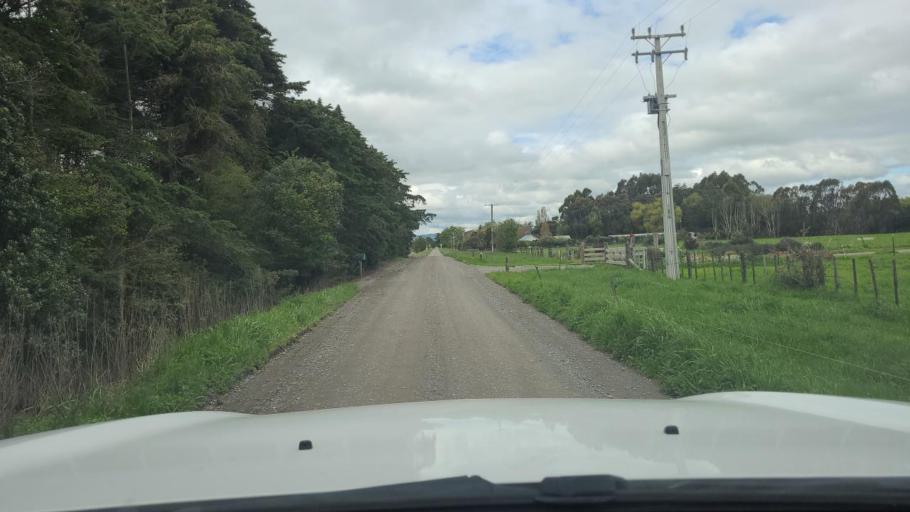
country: NZ
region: Wellington
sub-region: South Wairarapa District
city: Waipawa
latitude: -41.1446
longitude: 175.3771
